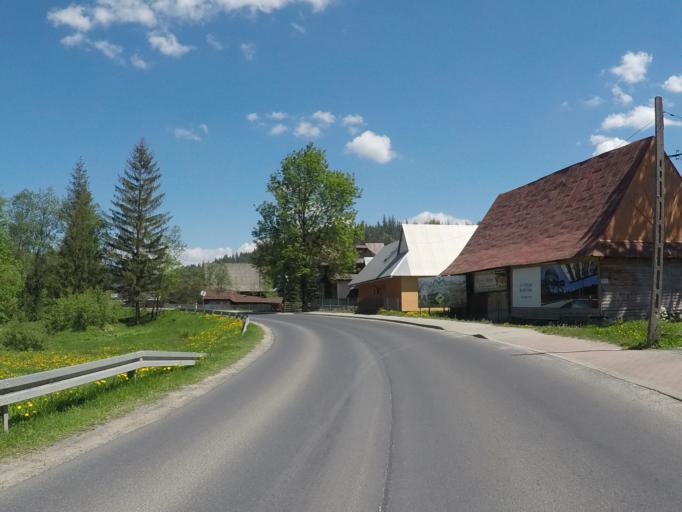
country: PL
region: Lesser Poland Voivodeship
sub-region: Powiat tatrzanski
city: Poronin
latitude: 49.3315
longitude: 20.0365
